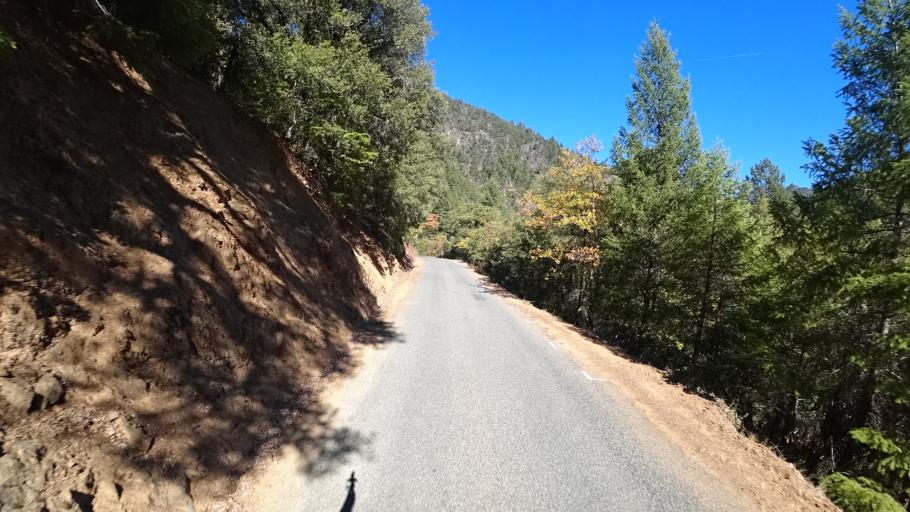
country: US
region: California
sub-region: Siskiyou County
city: Happy Camp
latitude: 41.2958
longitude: -123.1040
